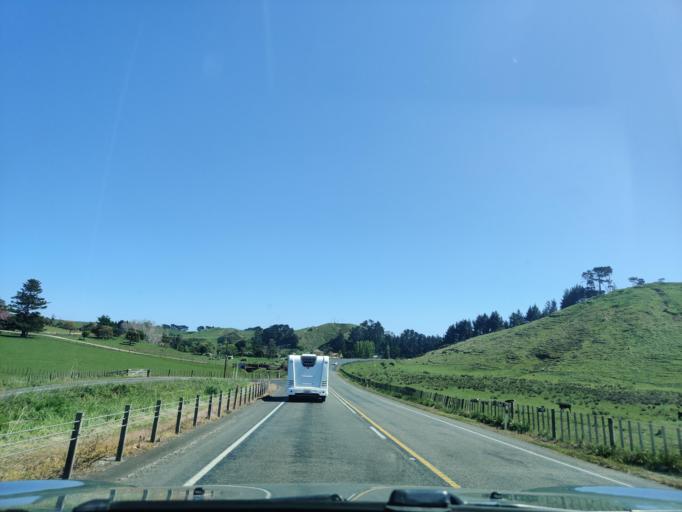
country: NZ
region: Taranaki
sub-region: South Taranaki District
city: Patea
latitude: -39.8095
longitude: 174.7396
